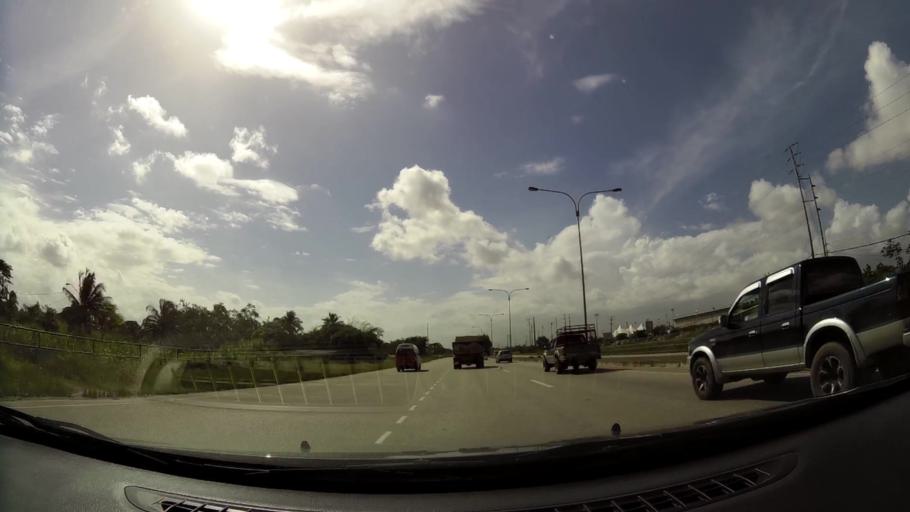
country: TT
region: Borough of Arima
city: Arima
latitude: 10.6074
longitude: -61.2737
